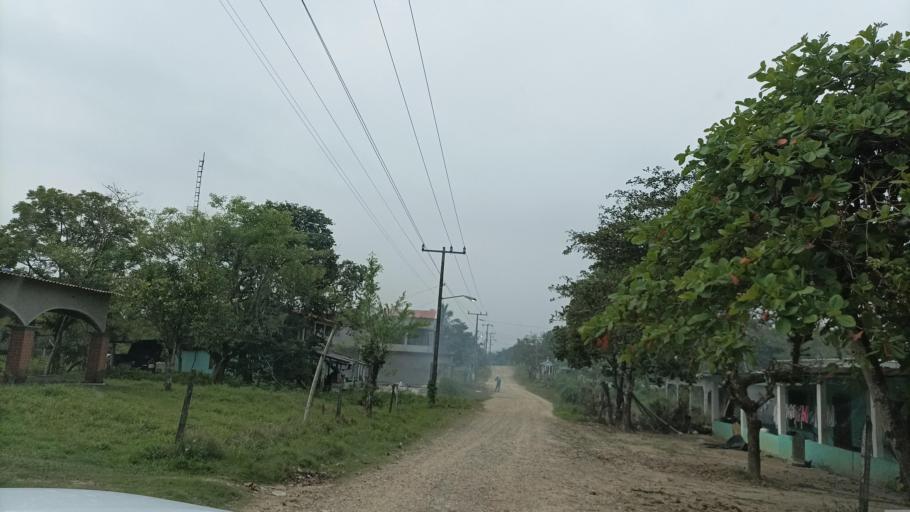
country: MX
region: Veracruz
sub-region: Uxpanapa
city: Poblado 10
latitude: 17.5417
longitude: -94.2387
